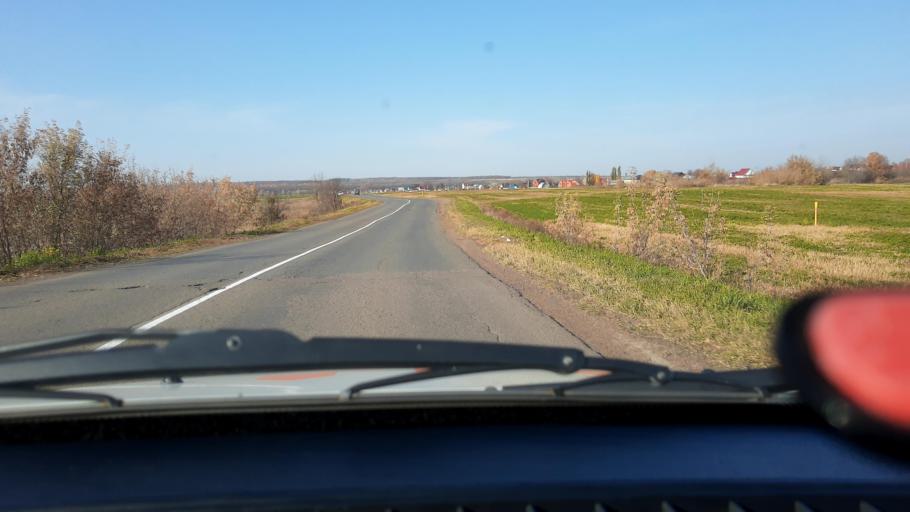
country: RU
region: Bashkortostan
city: Mikhaylovka
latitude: 54.8287
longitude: 55.9668
